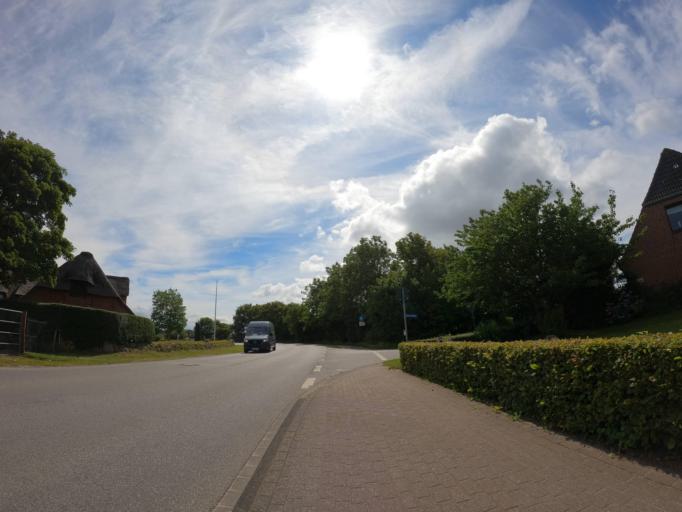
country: DE
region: Schleswig-Holstein
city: Sylt-Ost
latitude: 54.8698
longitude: 8.4389
